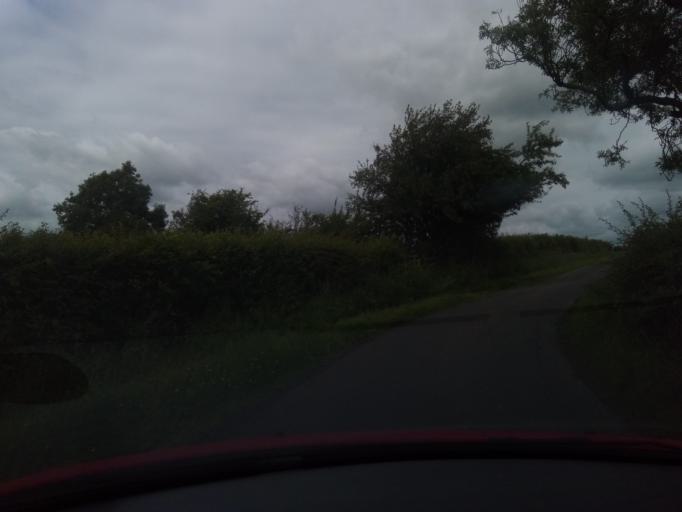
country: GB
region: Scotland
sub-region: The Scottish Borders
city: Hawick
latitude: 55.4552
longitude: -2.7448
